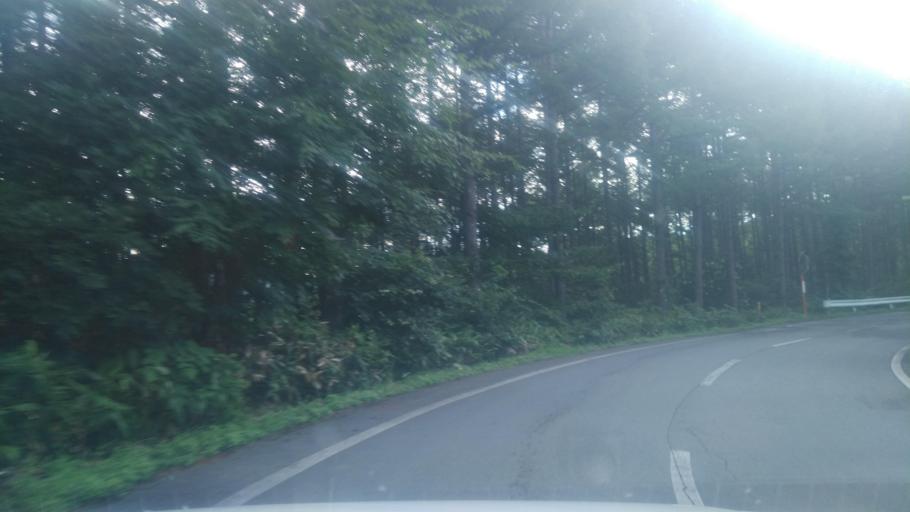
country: JP
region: Nagano
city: Ueda
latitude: 36.5103
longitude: 138.3658
